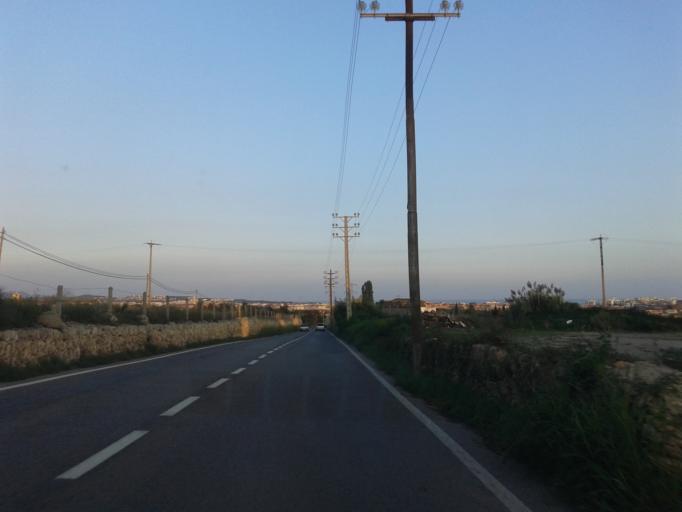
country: ES
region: Catalonia
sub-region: Provincia de Barcelona
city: Vilanova i la Geltru
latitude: 41.2291
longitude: 1.7003
